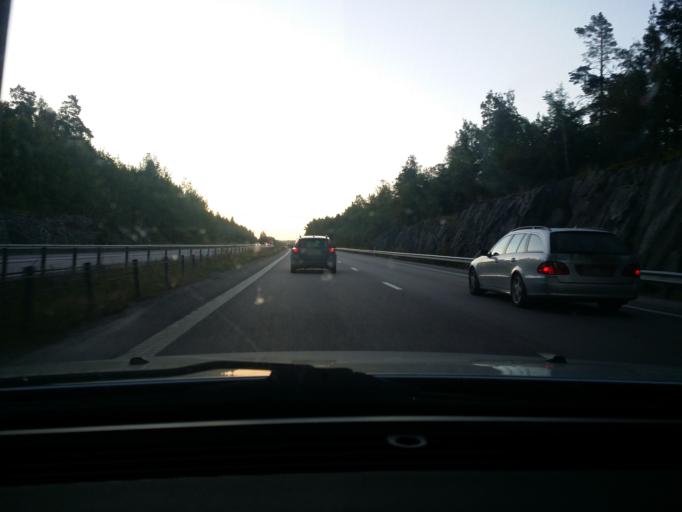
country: SE
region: Uppsala
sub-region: Enkopings Kommun
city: Enkoping
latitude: 59.6510
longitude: 17.1161
